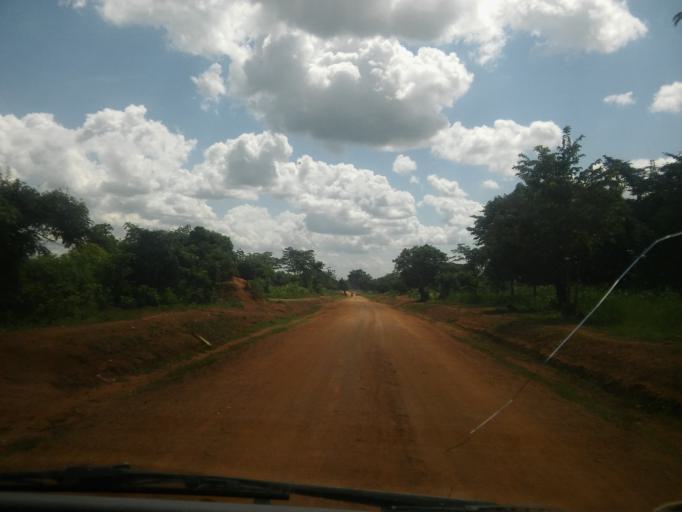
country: UG
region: Eastern Region
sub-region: Pallisa District
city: Pallisa
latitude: 1.1533
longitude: 33.8028
